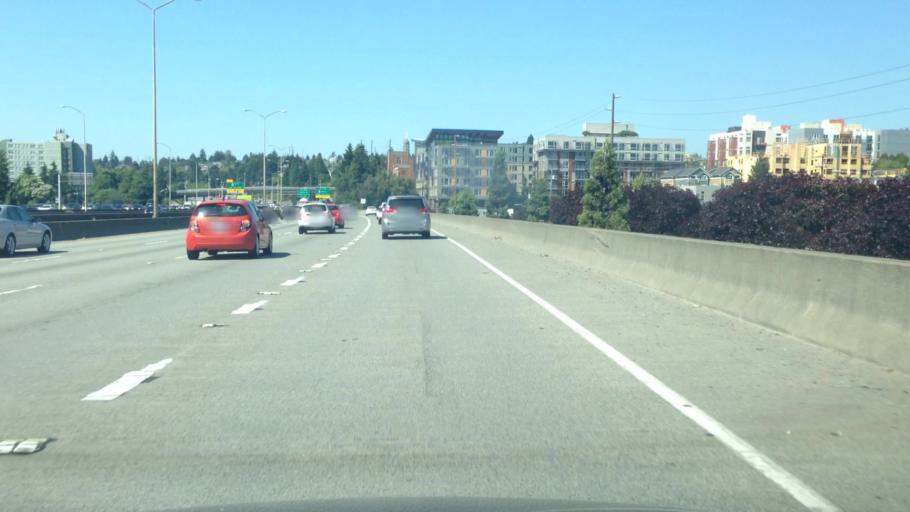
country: US
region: Washington
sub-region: King County
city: Seattle
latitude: 47.6748
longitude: -122.3206
